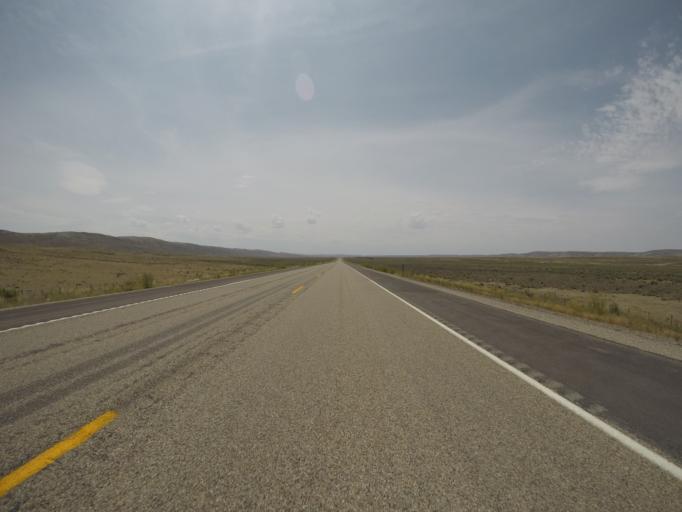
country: US
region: Wyoming
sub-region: Lincoln County
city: Kemmerer
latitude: 41.6889
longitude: -110.5673
